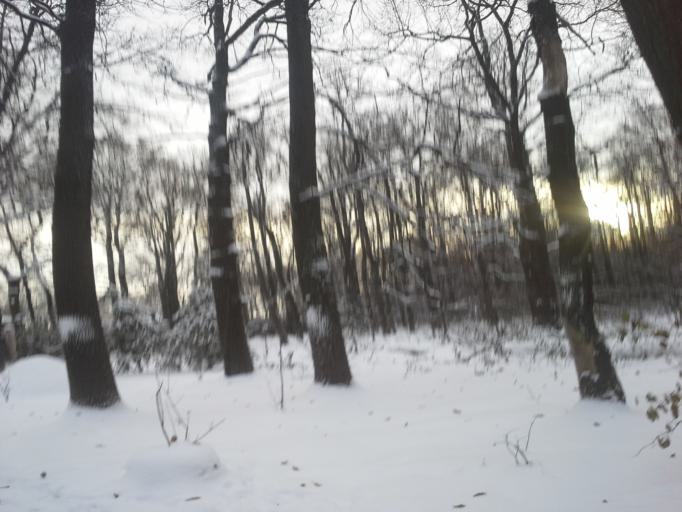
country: RU
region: Moskovskaya
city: Kommunarka
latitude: 55.5780
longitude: 37.4966
